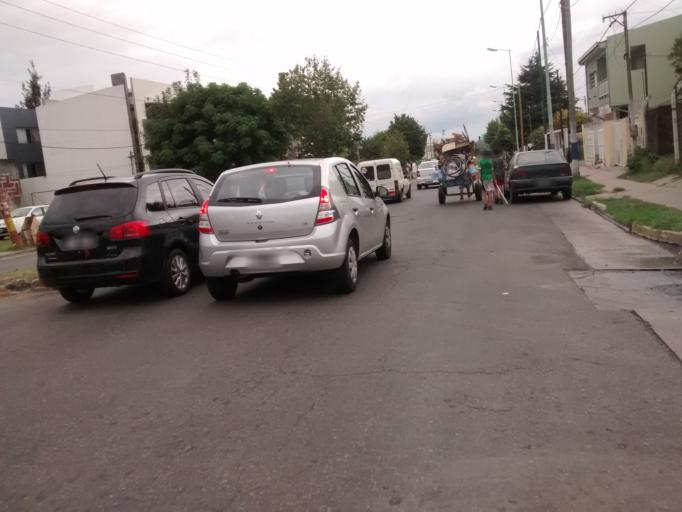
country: AR
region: Buenos Aires
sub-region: Partido de La Plata
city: La Plata
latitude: -34.9381
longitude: -57.9185
